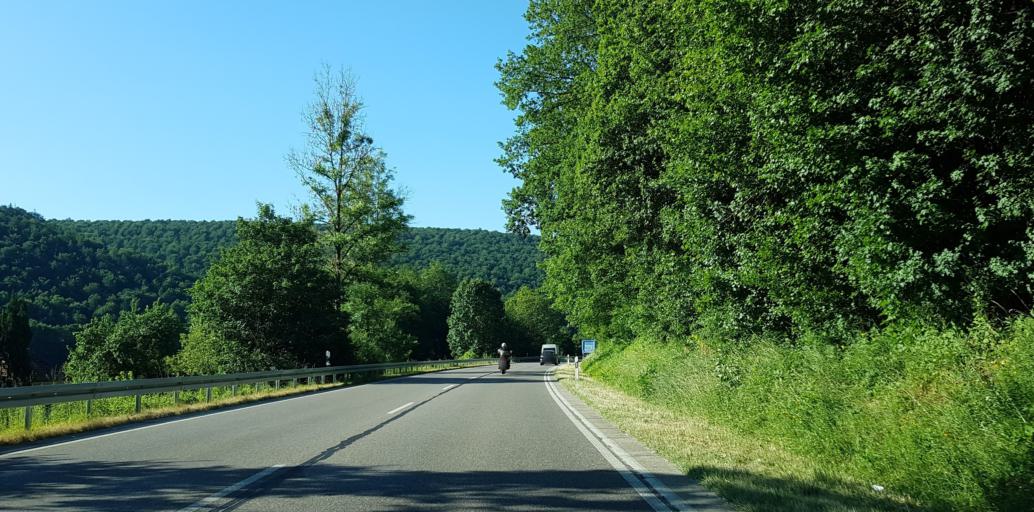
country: DE
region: Baden-Wuerttemberg
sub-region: Tuebingen Region
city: Blaubeuren
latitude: 48.3930
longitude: 9.7679
